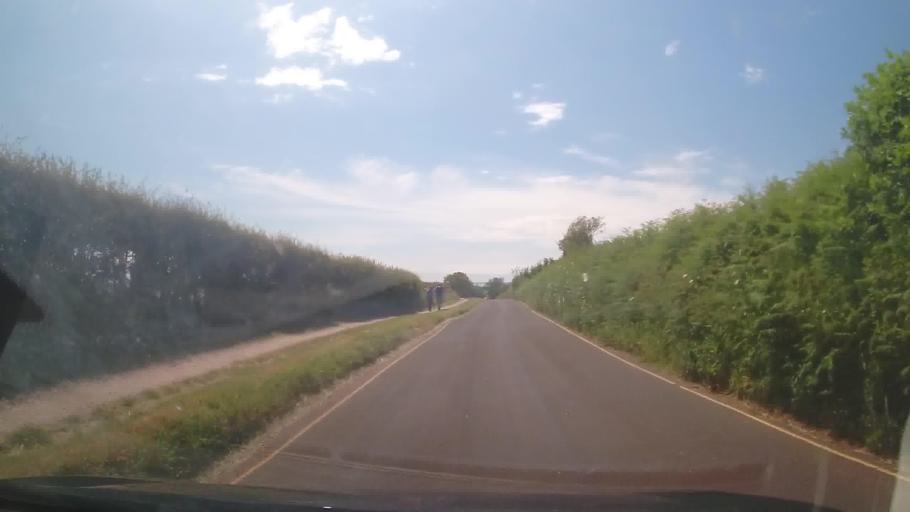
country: GB
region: England
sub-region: Devon
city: Dartmouth
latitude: 50.2899
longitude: -3.6503
